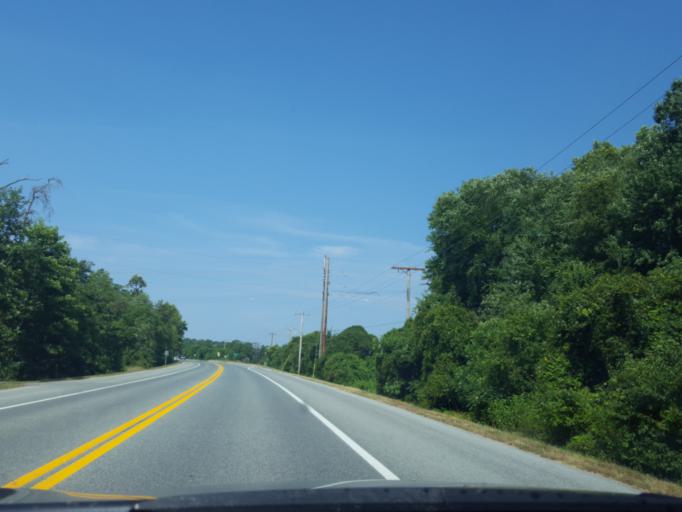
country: US
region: Maryland
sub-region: Saint Mary's County
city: Charlotte Hall
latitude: 38.4749
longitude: -76.7934
